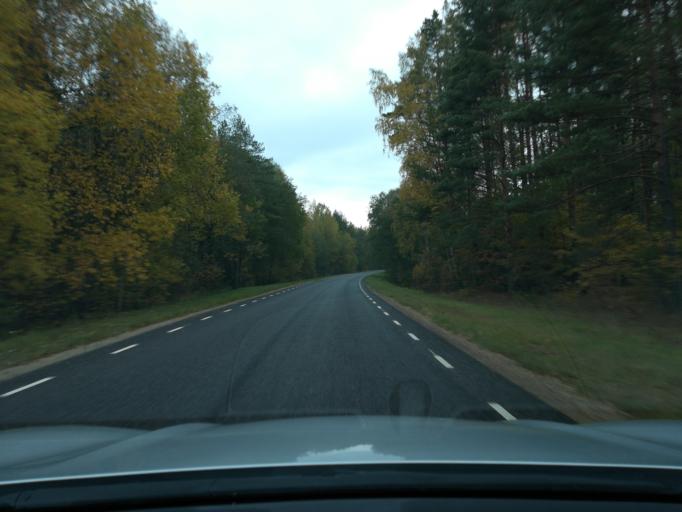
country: EE
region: Ida-Virumaa
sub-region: Johvi vald
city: Johvi
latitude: 59.0257
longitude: 27.3945
